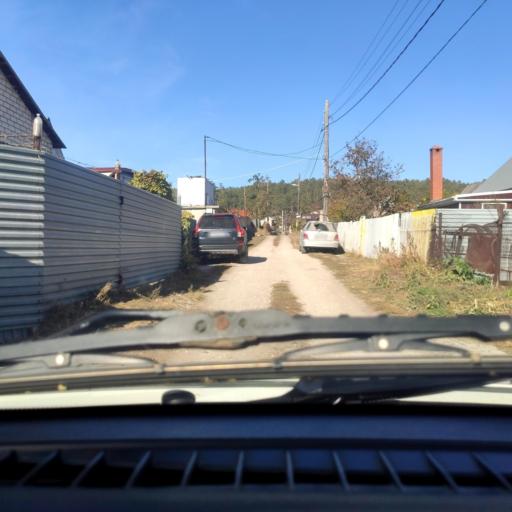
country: RU
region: Samara
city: Zhigulevsk
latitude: 53.4677
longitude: 49.5880
